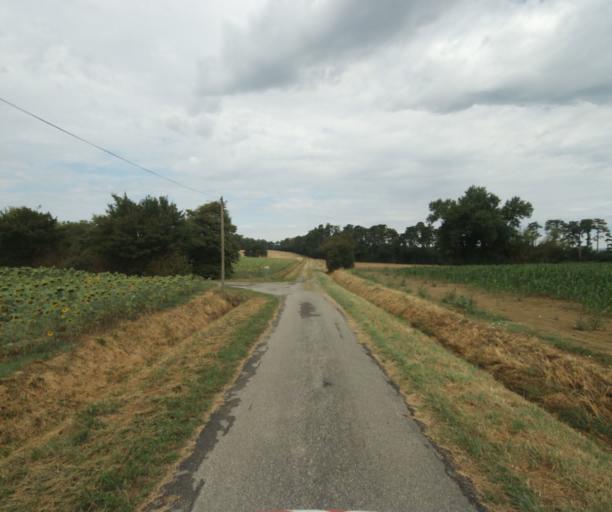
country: FR
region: Midi-Pyrenees
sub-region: Departement de la Haute-Garonne
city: Revel
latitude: 43.4416
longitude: 1.9584
